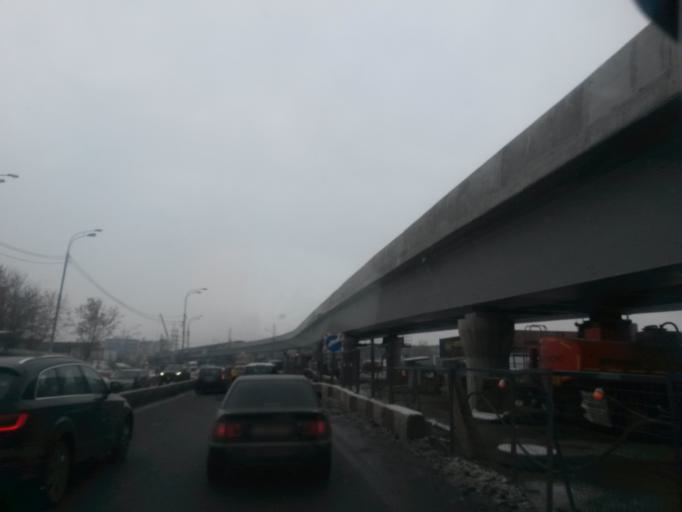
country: RU
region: Moskovskaya
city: Bol'shaya Setun'
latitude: 55.7037
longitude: 37.4205
